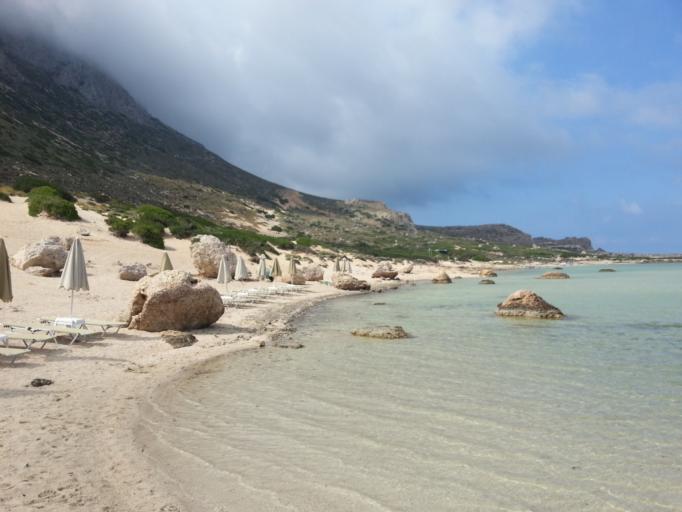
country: GR
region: Crete
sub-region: Nomos Chanias
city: Kissamos
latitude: 35.5815
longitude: 23.5909
